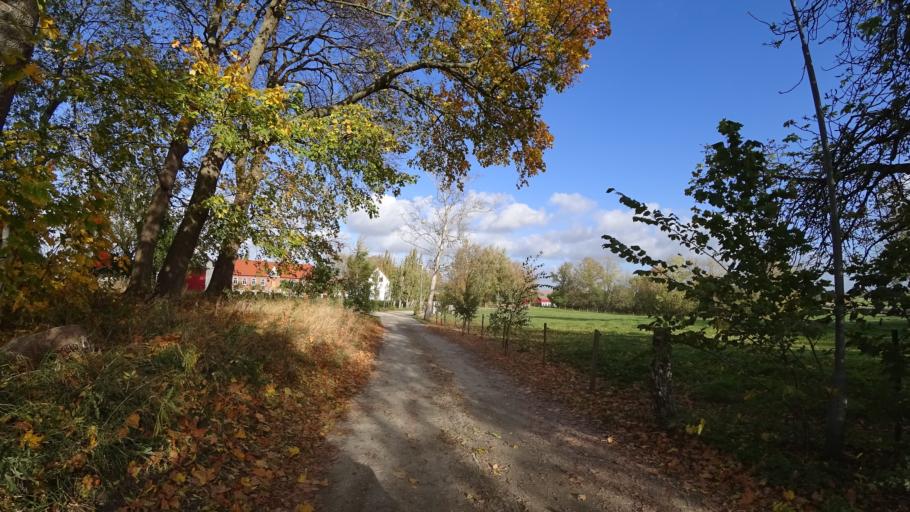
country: SE
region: Skane
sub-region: Staffanstorps Kommun
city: Hjaerup
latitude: 55.6292
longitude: 13.1447
